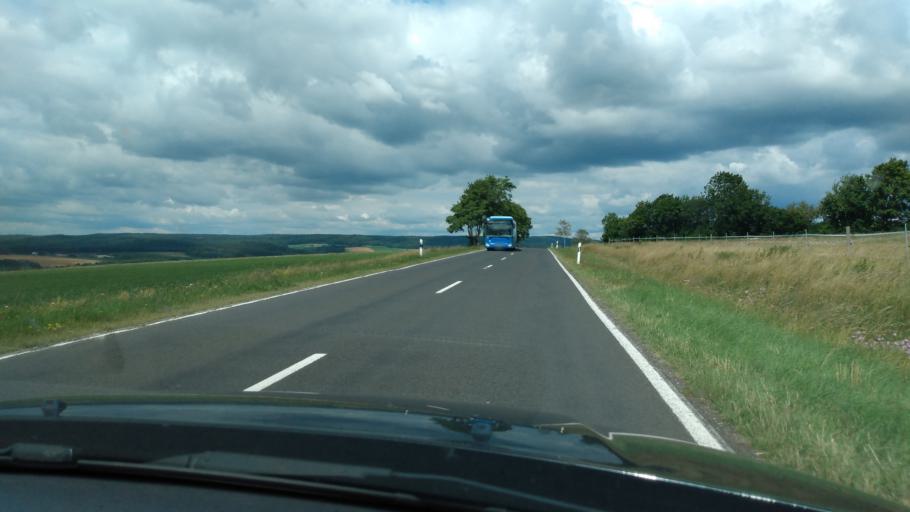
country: DE
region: Rheinland-Pfalz
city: Musweiler
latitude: 50.0178
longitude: 6.8122
